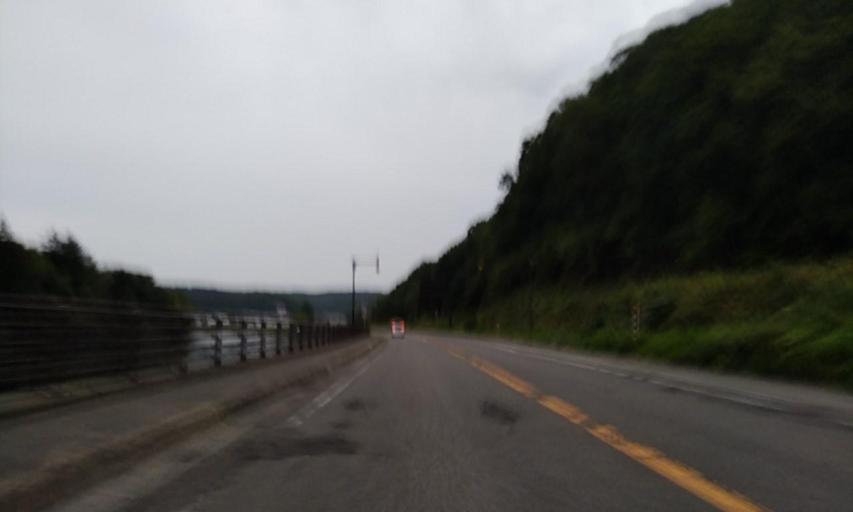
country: JP
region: Hokkaido
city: Abashiri
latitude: 44.0068
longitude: 144.2316
